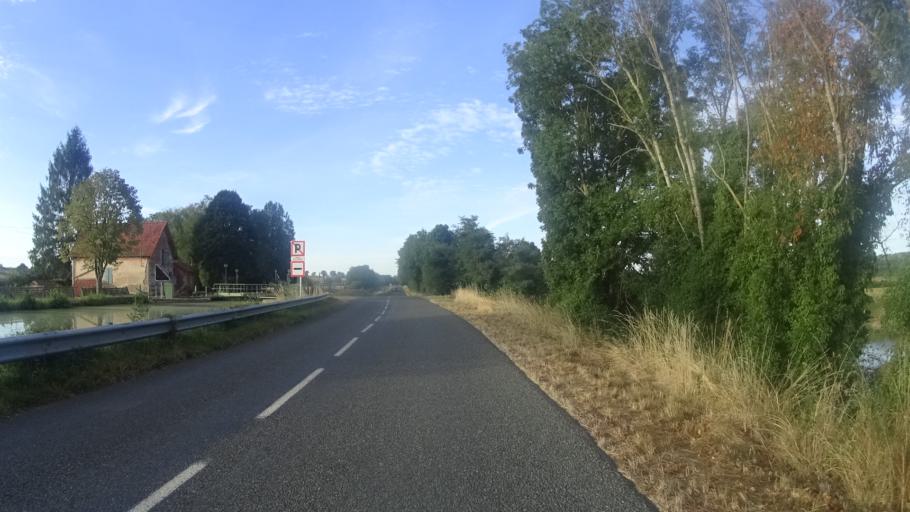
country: FR
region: Bourgogne
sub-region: Departement de Saone-et-Loire
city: Palinges
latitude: 46.5035
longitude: 4.1851
